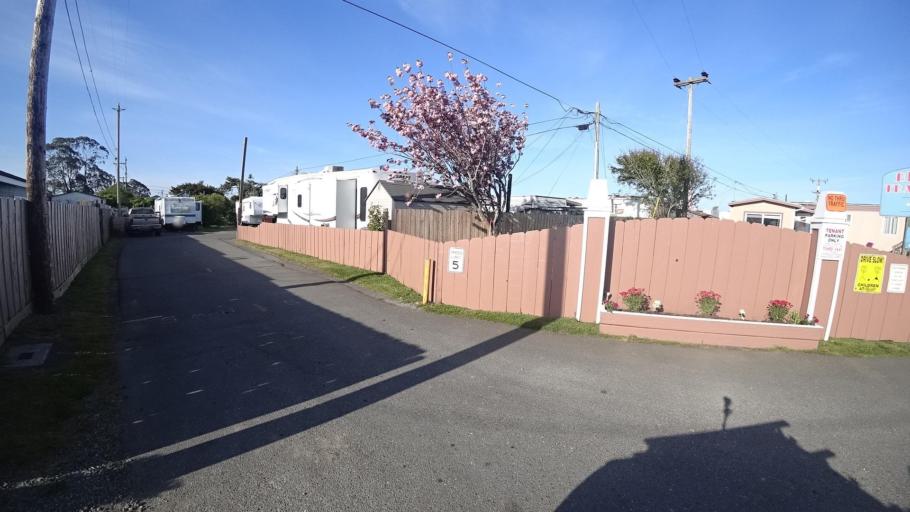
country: US
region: California
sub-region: Humboldt County
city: Bayview
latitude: 40.7742
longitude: -124.1920
